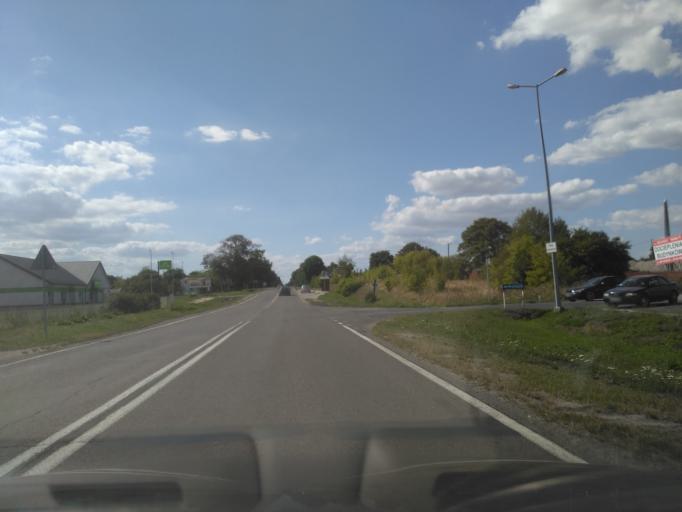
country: PL
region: Lublin Voivodeship
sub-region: Powiat swidnicki
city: Piaski
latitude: 51.1418
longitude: 22.8315
